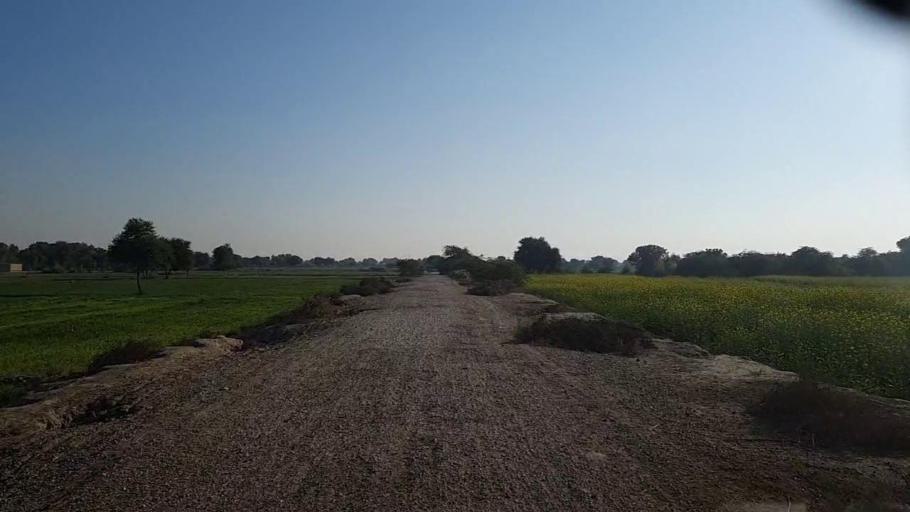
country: PK
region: Sindh
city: Darya Khan Marri
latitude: 26.6903
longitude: 68.3625
